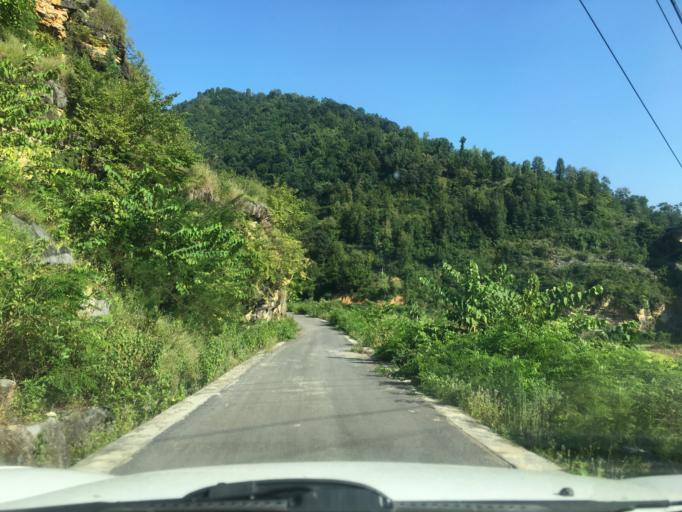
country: CN
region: Guangxi Zhuangzu Zizhiqu
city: Xinzhou
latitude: 25.4577
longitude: 105.7341
